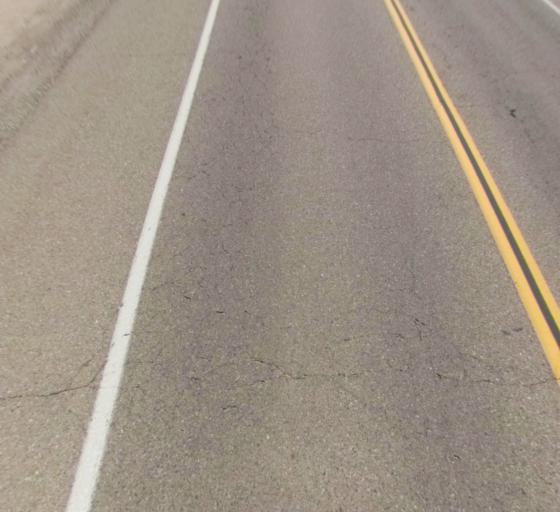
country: US
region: California
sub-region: Fresno County
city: Biola
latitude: 36.8501
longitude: -120.0805
